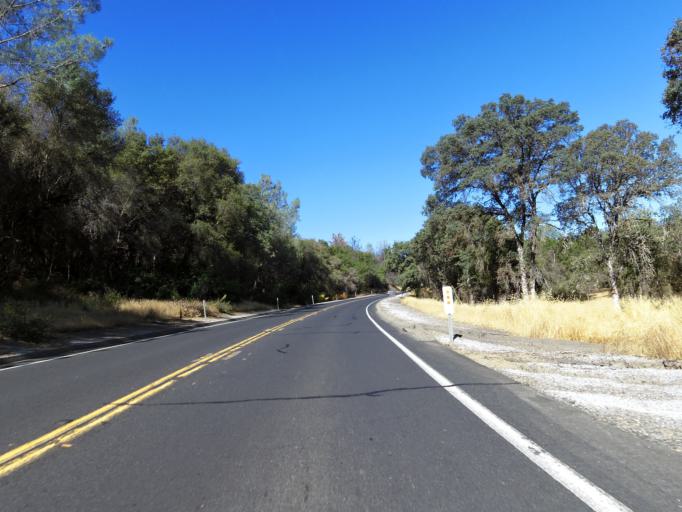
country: US
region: California
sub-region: Mariposa County
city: Mariposa
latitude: 37.4763
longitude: -120.0368
